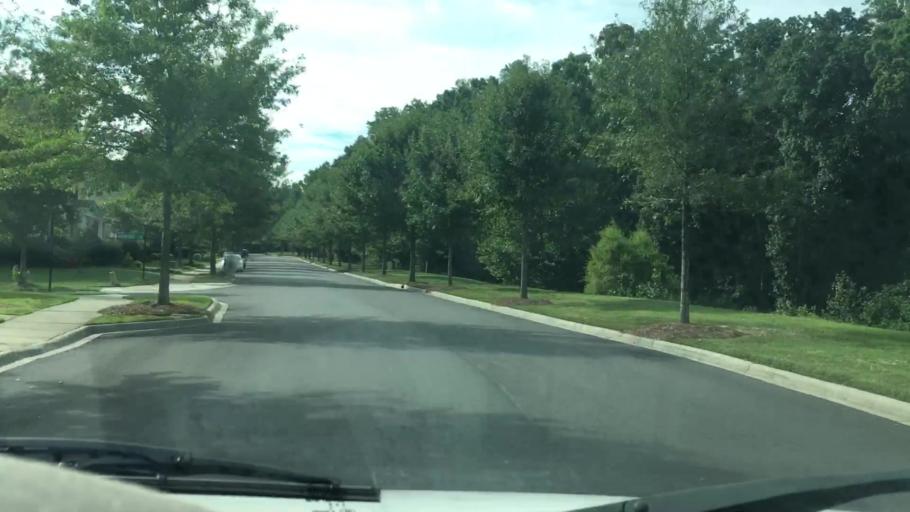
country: US
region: North Carolina
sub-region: Mecklenburg County
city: Huntersville
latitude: 35.4468
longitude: -80.7765
